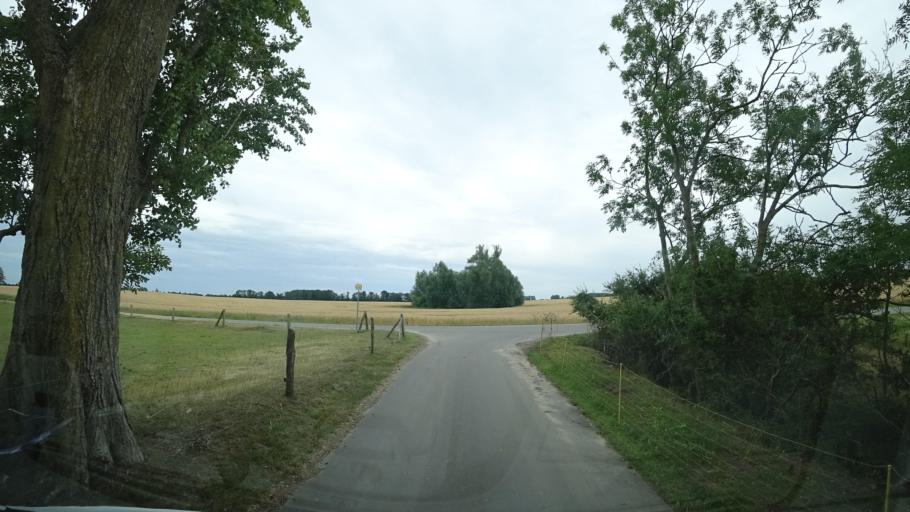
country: DE
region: Mecklenburg-Vorpommern
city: Rambin
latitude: 54.3244
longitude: 13.2080
